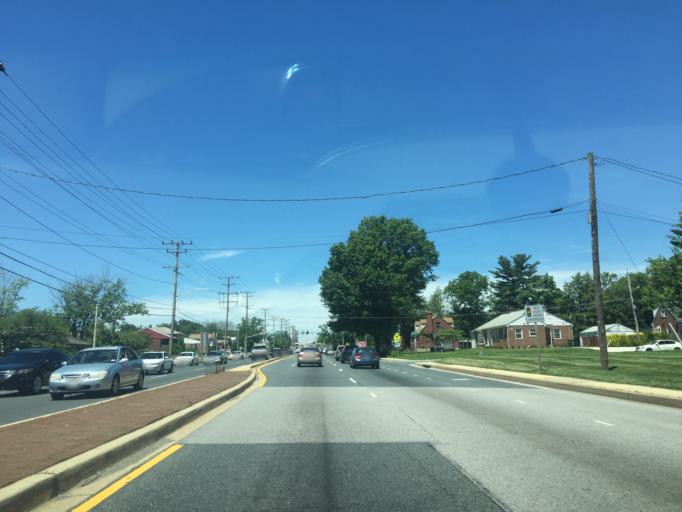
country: US
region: Maryland
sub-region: Baltimore County
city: Milford Mill
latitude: 39.3503
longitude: -76.7485
